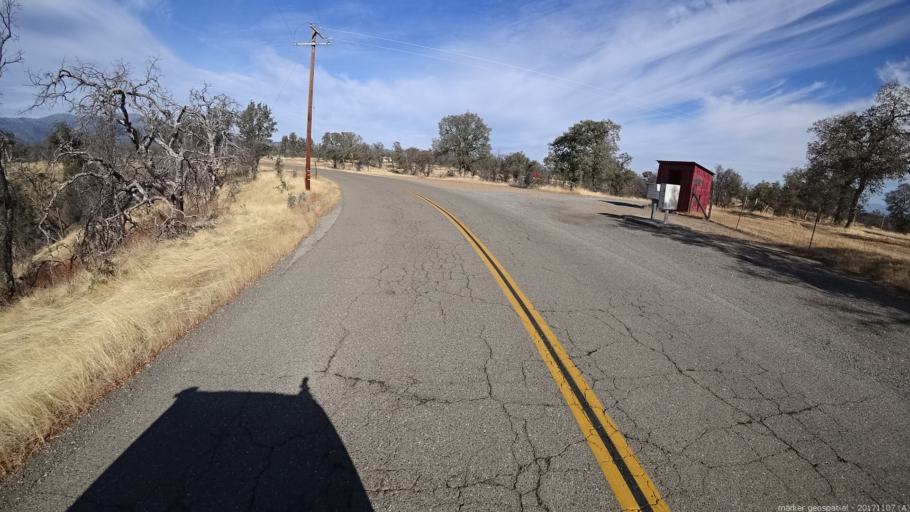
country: US
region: California
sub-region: Shasta County
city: Shasta
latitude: 40.4610
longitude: -122.5361
